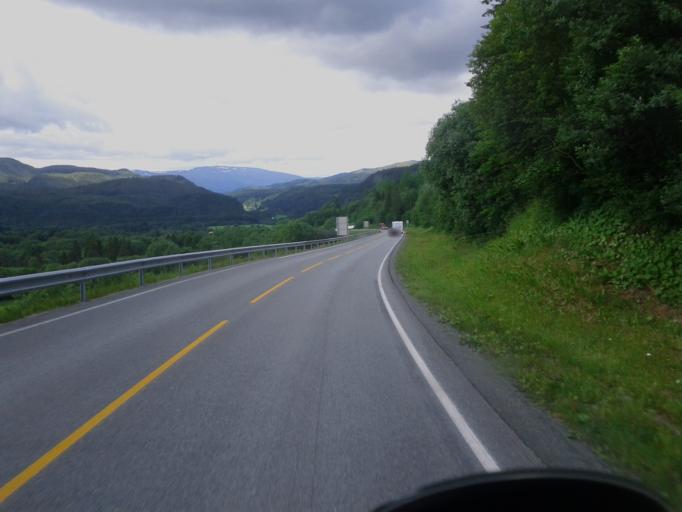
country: NO
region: Nord-Trondelag
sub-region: Grong
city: Grong
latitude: 64.5359
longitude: 12.4160
